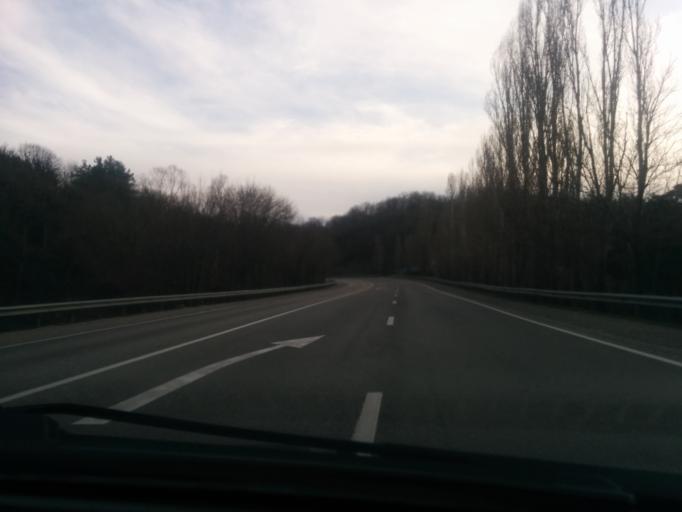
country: RU
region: Krasnodarskiy
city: Ol'ginka
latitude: 44.1922
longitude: 38.8890
